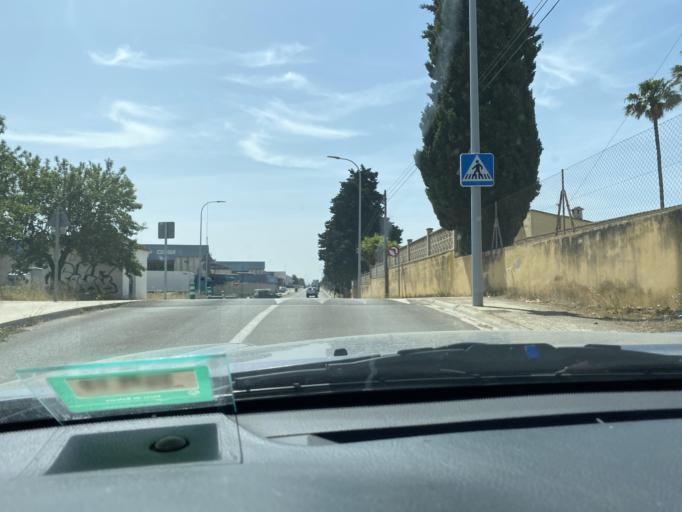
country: ES
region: Balearic Islands
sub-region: Illes Balears
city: Marratxi
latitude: 39.6226
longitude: 2.7115
